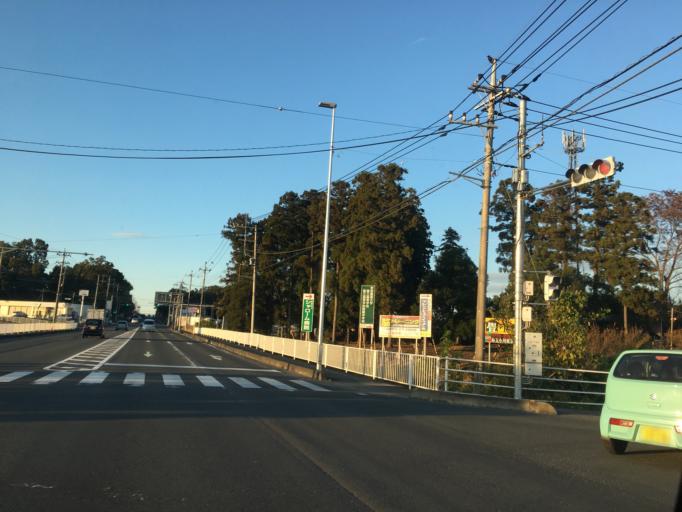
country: JP
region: Saitama
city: Fukiage-fujimi
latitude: 36.0459
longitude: 139.4137
